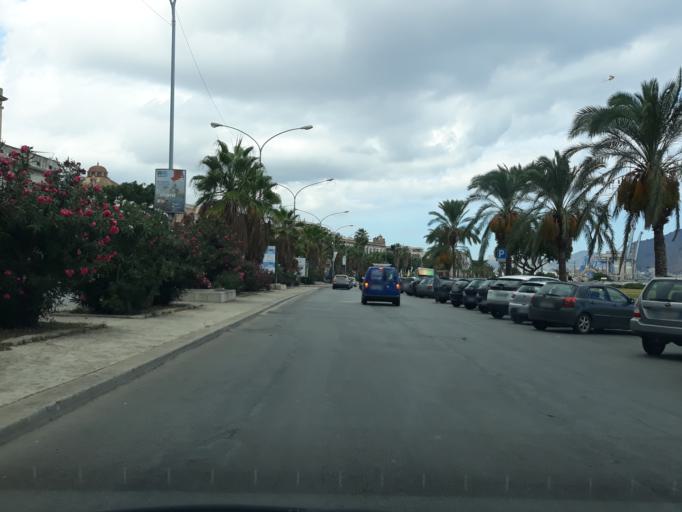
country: IT
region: Sicily
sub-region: Palermo
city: Palermo
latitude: 38.1159
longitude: 13.3752
